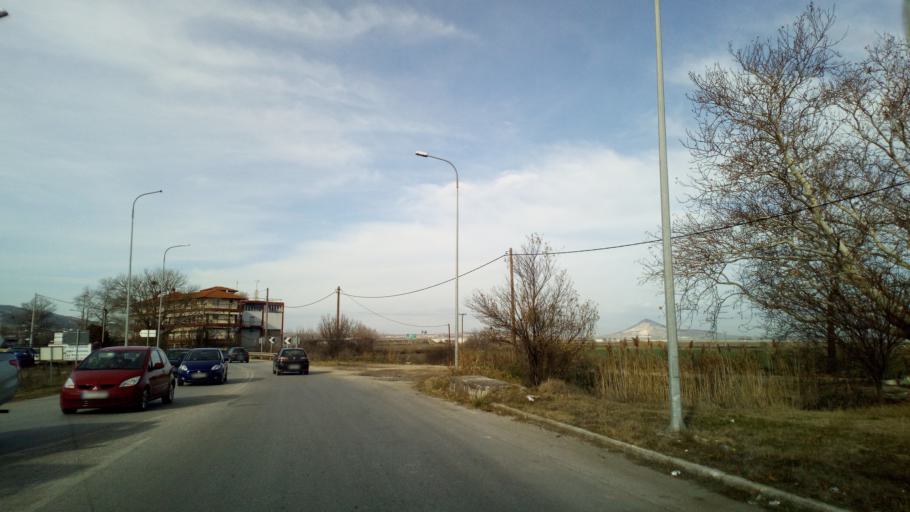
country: GR
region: Central Macedonia
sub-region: Nomos Thessalonikis
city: Lagyna
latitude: 40.7308
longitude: 23.0183
